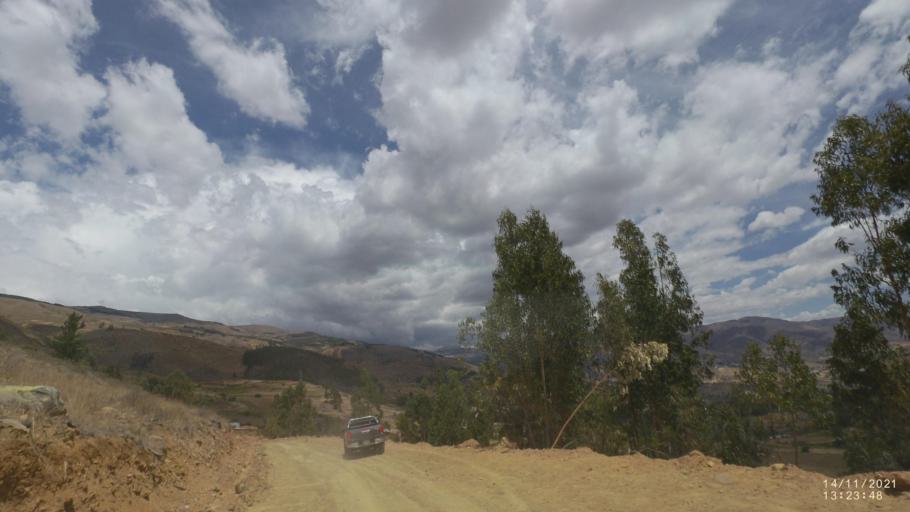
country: BO
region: Cochabamba
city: Colomi
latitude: -17.3774
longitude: -65.9824
